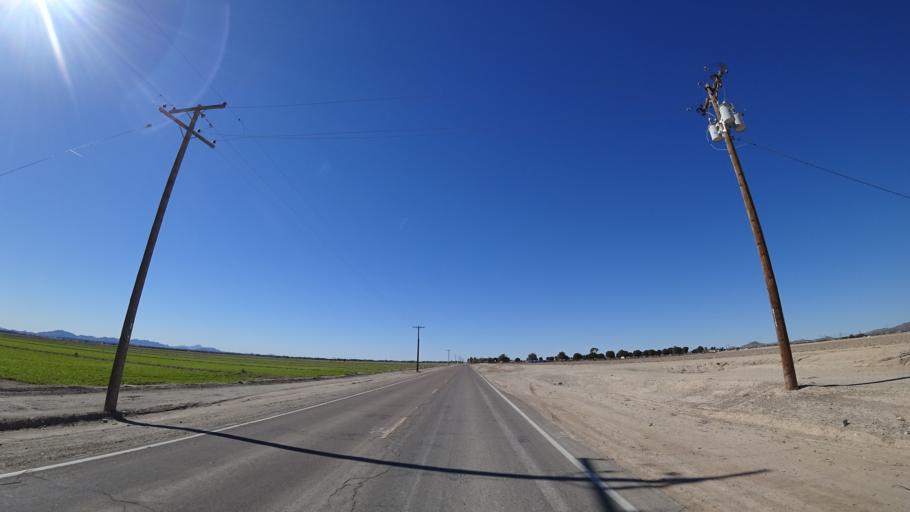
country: US
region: Arizona
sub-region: Maricopa County
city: Buckeye
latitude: 33.4067
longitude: -112.5422
